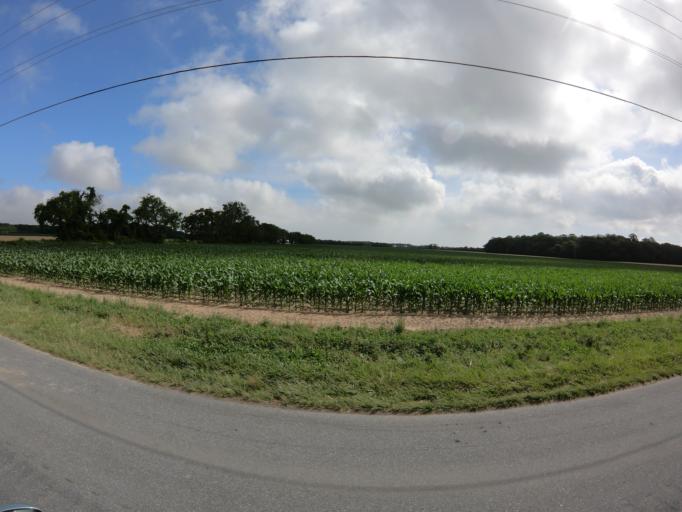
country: US
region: Delaware
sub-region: Sussex County
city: Lewes
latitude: 38.7666
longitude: -75.2127
